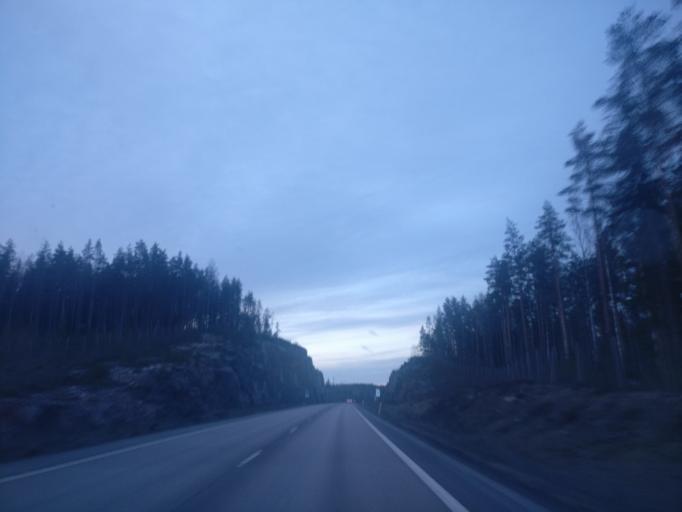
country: FI
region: Central Finland
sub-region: Jyvaeskylae
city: Saeynaetsalo
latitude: 62.2046
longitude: 25.8903
